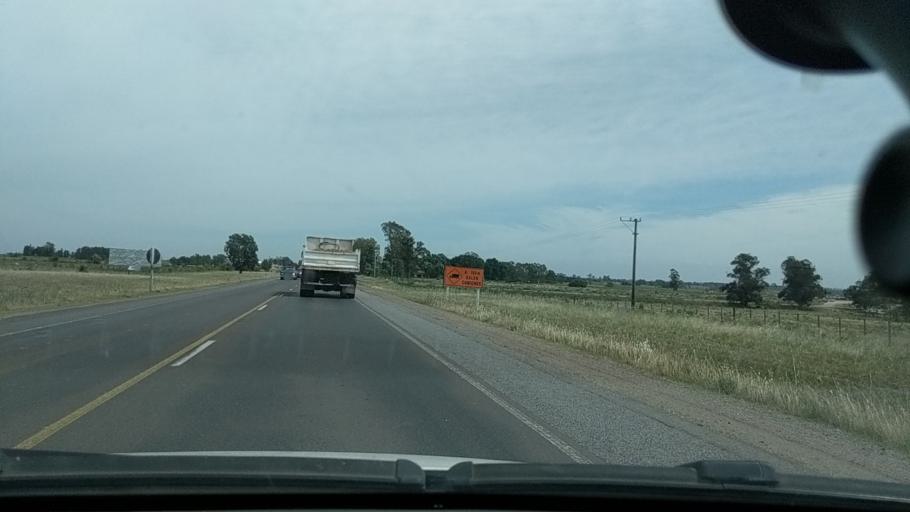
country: UY
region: Durazno
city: Durazno
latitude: -33.4300
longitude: -56.4955
